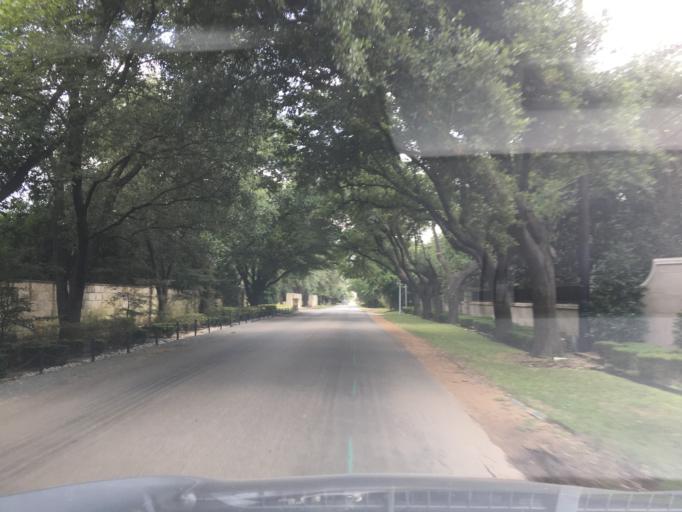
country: US
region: Texas
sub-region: Dallas County
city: University Park
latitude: 32.8927
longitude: -96.8247
